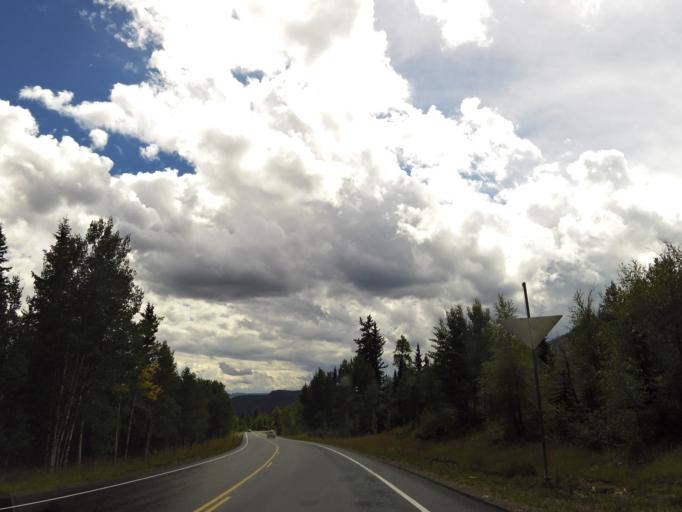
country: US
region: Colorado
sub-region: San Juan County
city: Silverton
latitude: 37.6645
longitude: -107.7981
